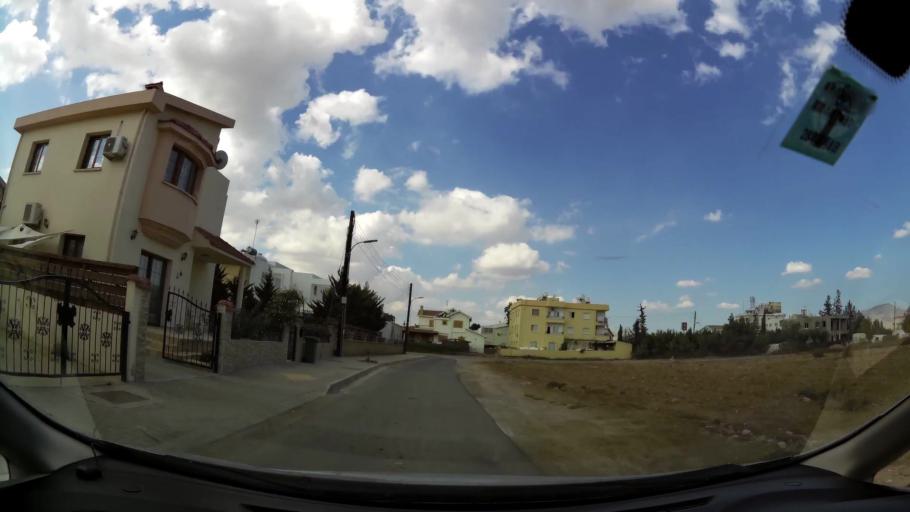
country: CY
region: Lefkosia
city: Nicosia
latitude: 35.2108
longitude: 33.3835
